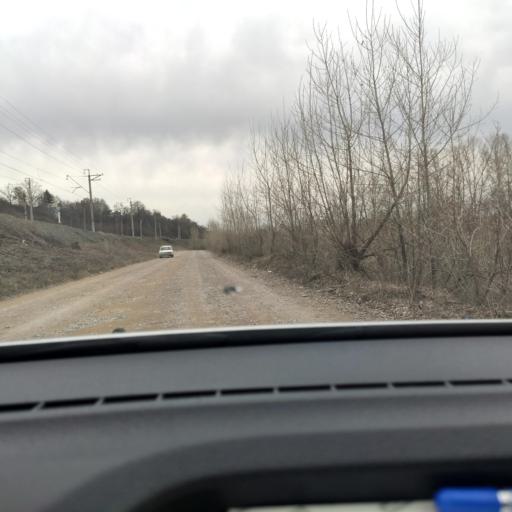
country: RU
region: Bashkortostan
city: Avdon
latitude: 54.6164
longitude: 55.6059
